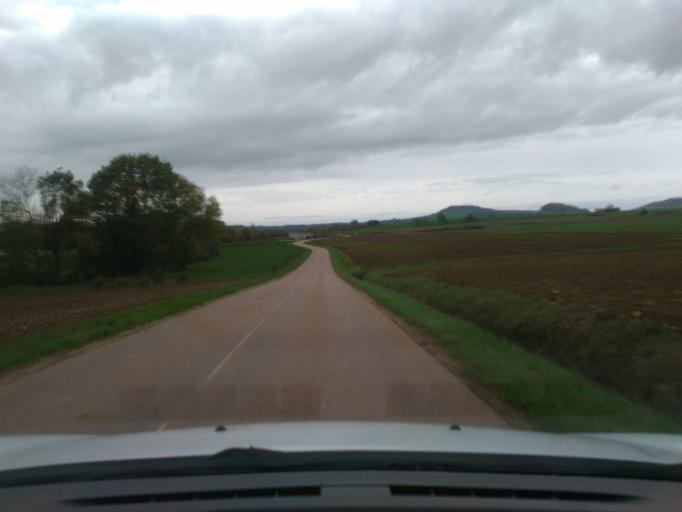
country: FR
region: Lorraine
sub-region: Departement des Vosges
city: Mirecourt
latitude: 48.3455
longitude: 6.1017
